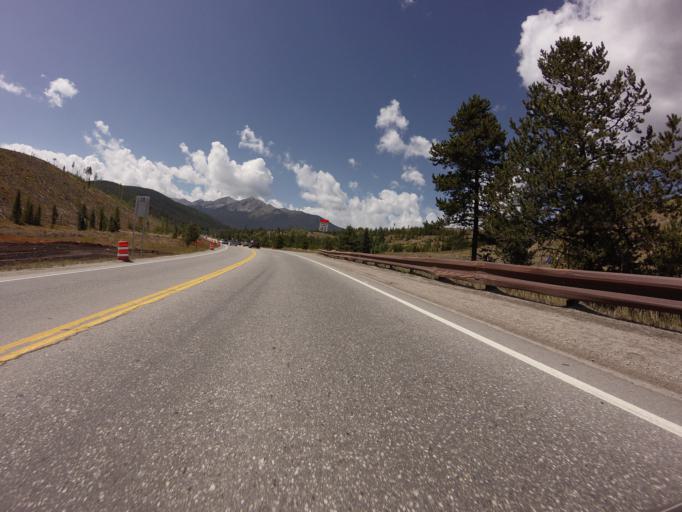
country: US
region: Colorado
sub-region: Summit County
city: Frisco
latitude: 39.5779
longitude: -106.0611
